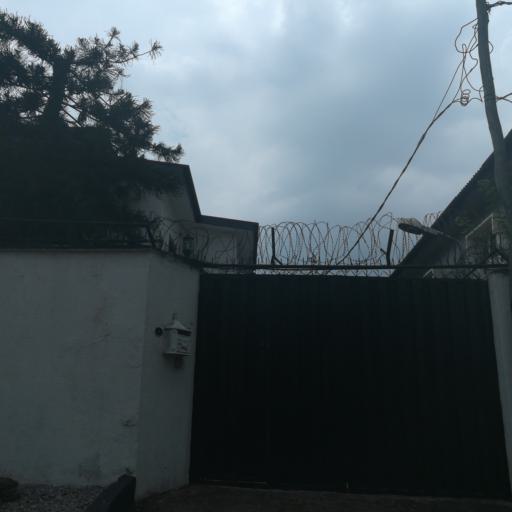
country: NG
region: Lagos
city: Ojota
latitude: 6.5738
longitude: 3.3914
